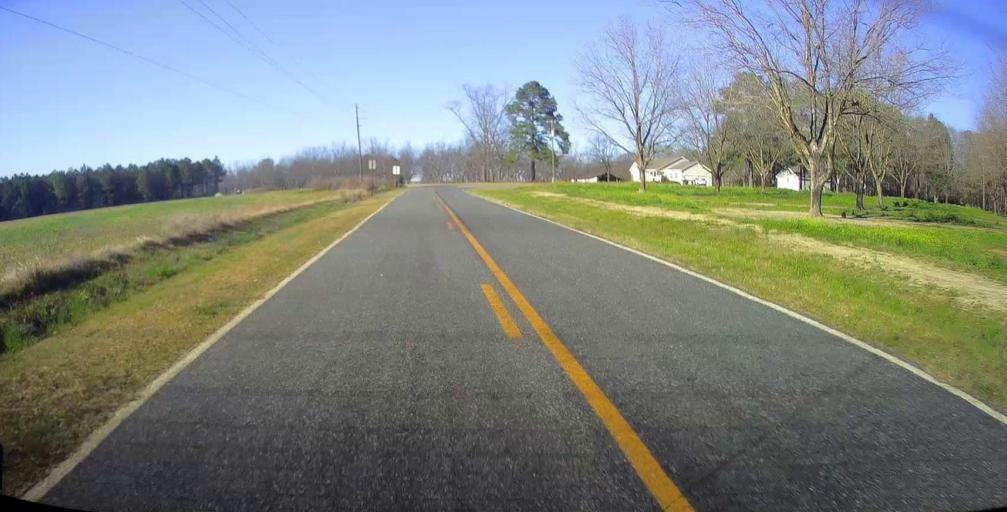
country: US
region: Georgia
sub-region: Peach County
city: Fort Valley
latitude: 32.6318
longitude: -83.8544
